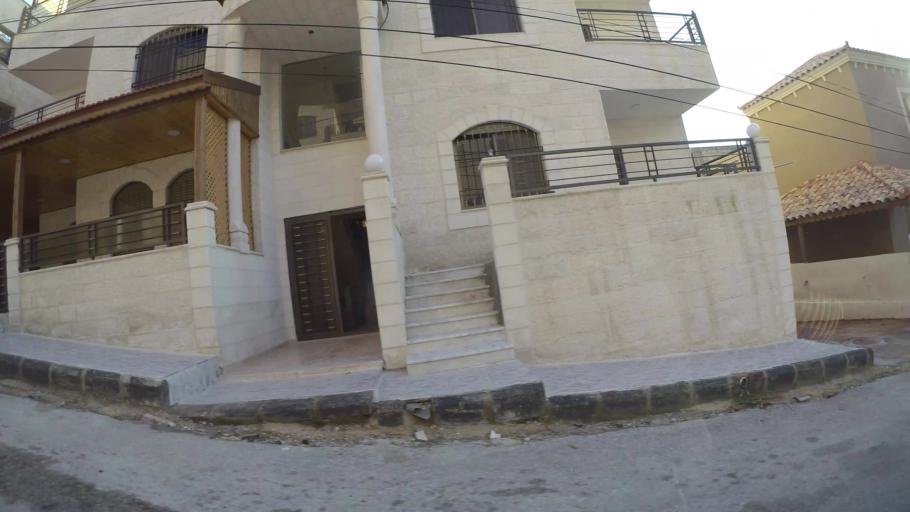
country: JO
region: Amman
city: Amman
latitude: 31.9840
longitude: 35.9601
